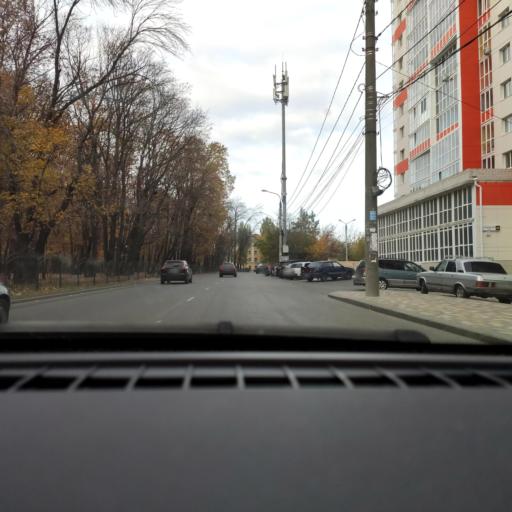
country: RU
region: Voronezj
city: Voronezh
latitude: 51.7092
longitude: 39.2298
